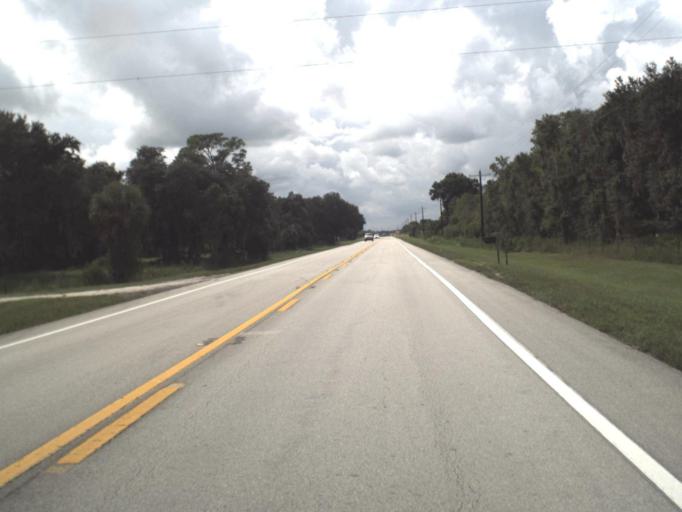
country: US
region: Florida
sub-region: DeSoto County
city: Nocatee
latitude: 27.2028
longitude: -82.0454
